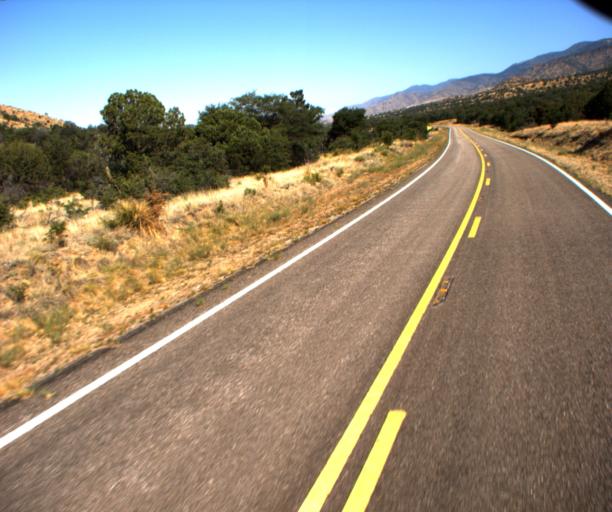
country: US
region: Arizona
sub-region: Graham County
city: Swift Trail Junction
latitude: 32.5935
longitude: -109.8563
